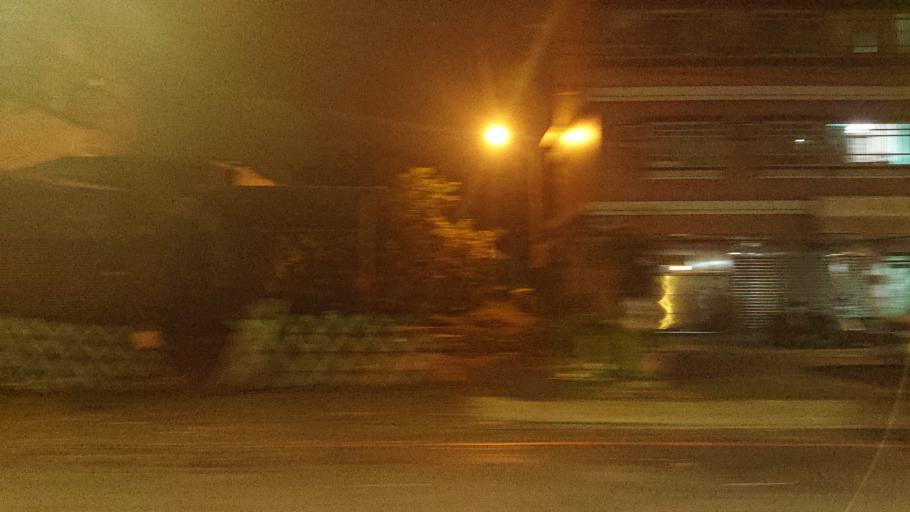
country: TW
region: Taipei
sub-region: Taipei
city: Banqiao
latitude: 24.9520
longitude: 121.4111
